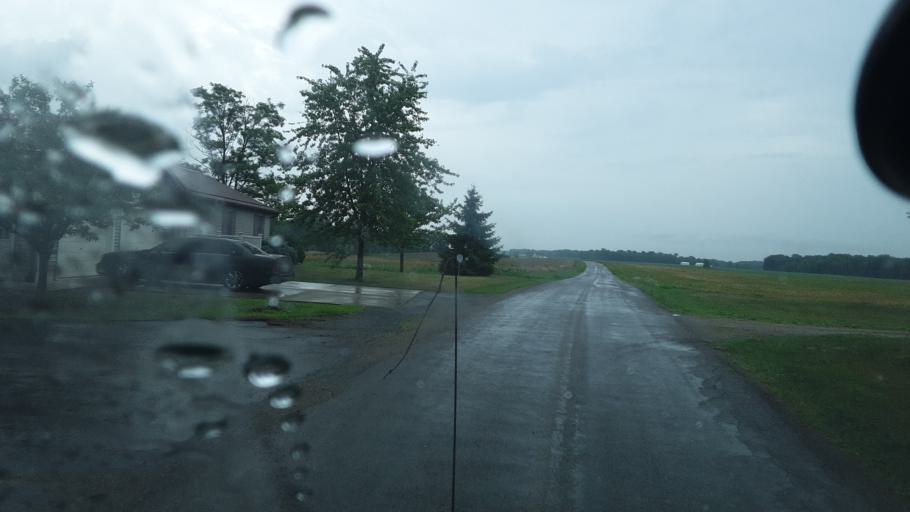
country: US
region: Ohio
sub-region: Williams County
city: Edgerton
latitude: 41.5245
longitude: -84.8045
